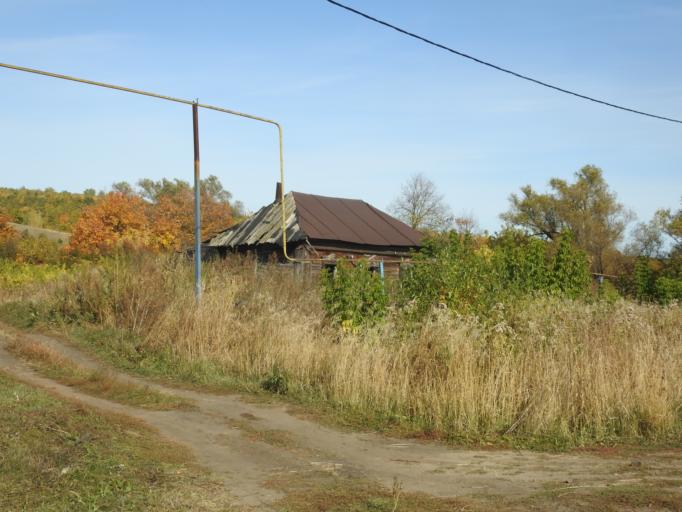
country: RU
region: Saratov
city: Baltay
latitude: 52.5182
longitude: 46.7776
